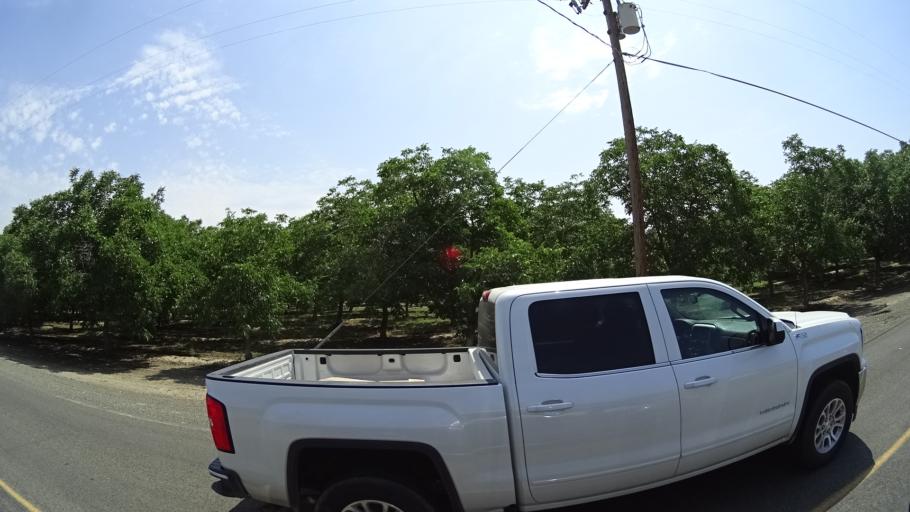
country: US
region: California
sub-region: Fresno County
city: Laton
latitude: 36.4000
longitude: -119.7450
